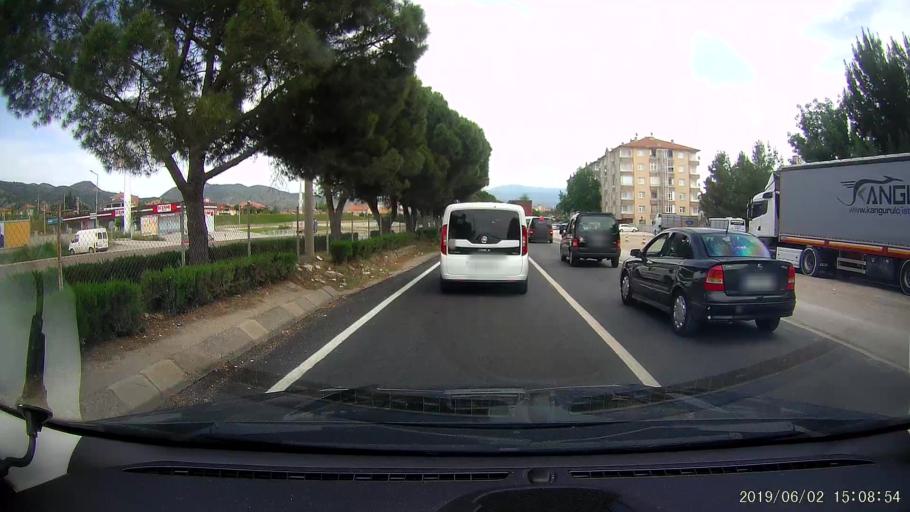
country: TR
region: Corum
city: Osmancik
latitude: 40.9791
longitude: 34.8037
